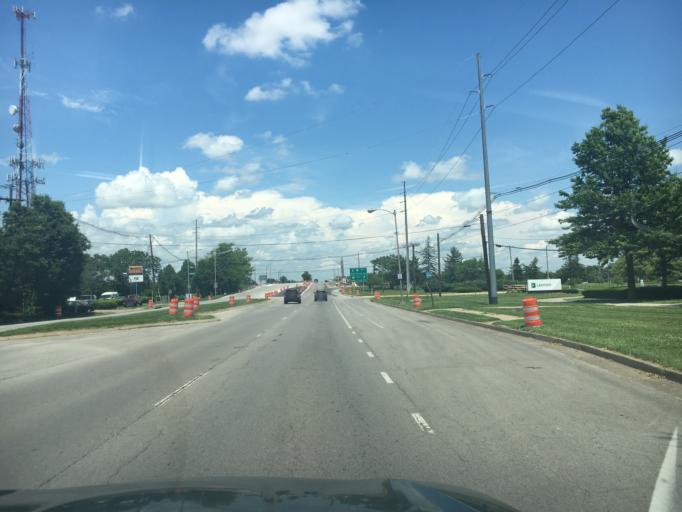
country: US
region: Kentucky
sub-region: Fayette County
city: Lexington-Fayette
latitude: 38.0710
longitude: -84.4966
